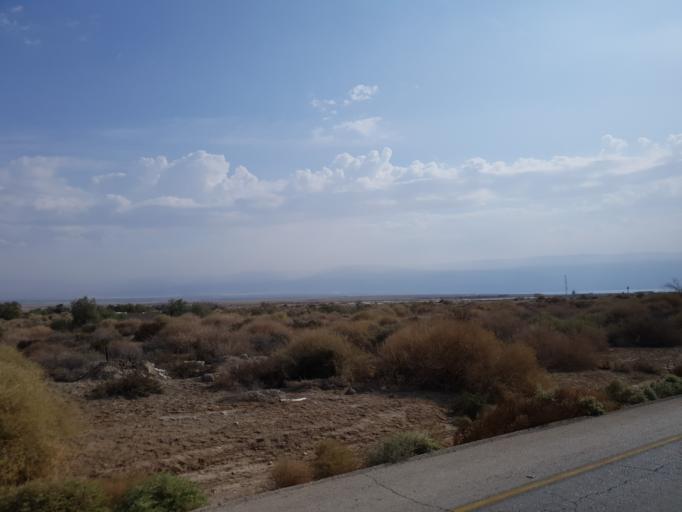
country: PS
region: West Bank
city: Jericho
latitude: 31.7812
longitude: 35.5022
